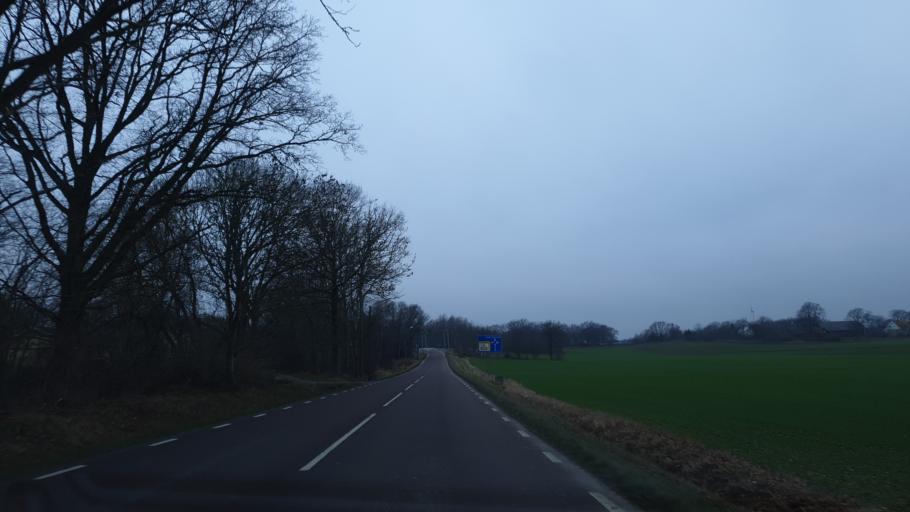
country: SE
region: Blekinge
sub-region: Karlskrona Kommun
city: Jaemjoe
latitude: 56.1681
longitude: 15.7456
